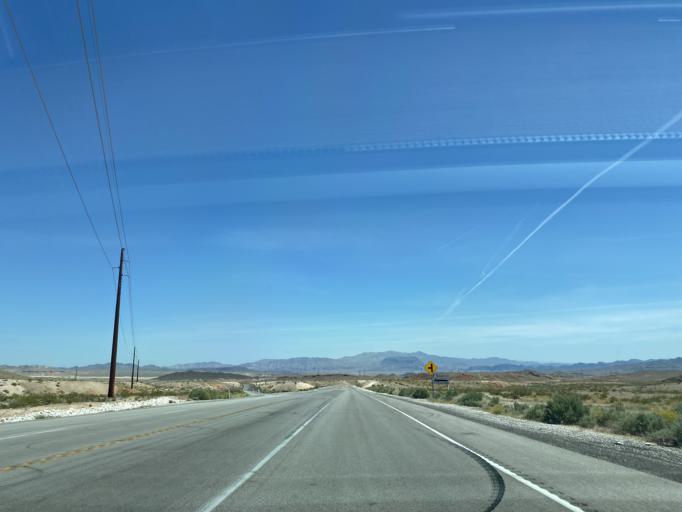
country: US
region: Nevada
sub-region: Clark County
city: Nellis Air Force Base
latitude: 36.2040
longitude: -114.9423
